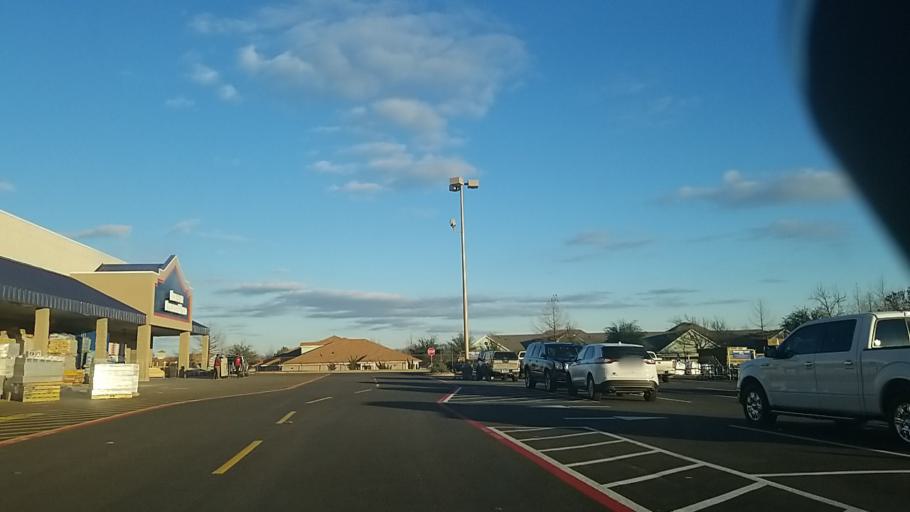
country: US
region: Texas
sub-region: Denton County
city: Denton
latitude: 33.1967
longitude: -97.0897
